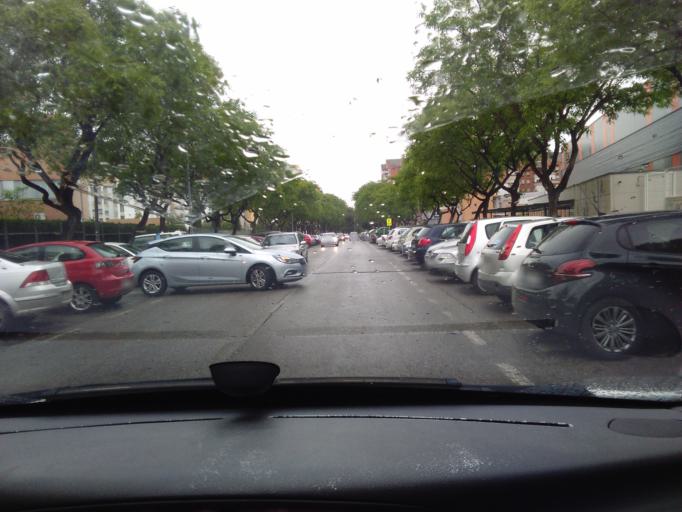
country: ES
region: Andalusia
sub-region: Provincia de Sevilla
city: Sevilla
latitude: 37.4002
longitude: -5.9384
